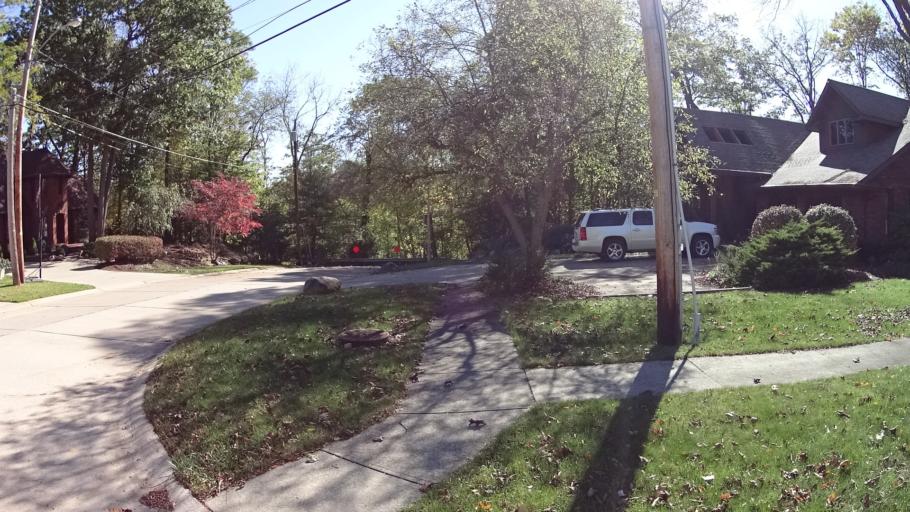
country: US
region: Ohio
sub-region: Lorain County
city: Amherst
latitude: 41.3911
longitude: -82.2360
